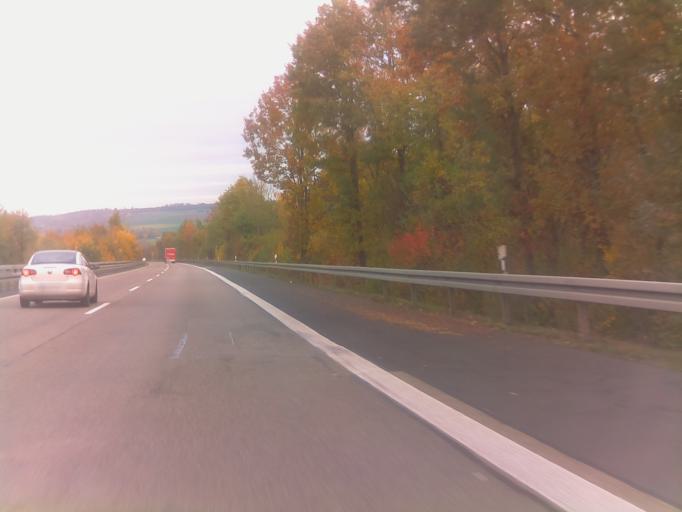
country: DE
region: Hesse
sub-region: Regierungsbezirk Darmstadt
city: Altenstadt
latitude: 50.2676
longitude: 8.9825
